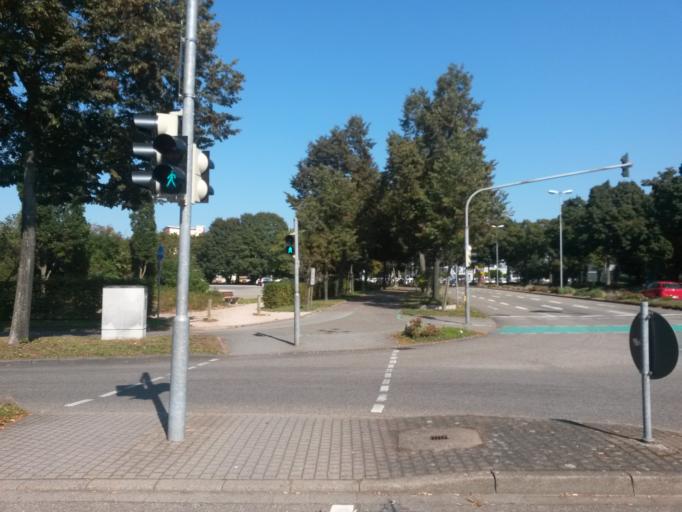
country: DE
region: Baden-Wuerttemberg
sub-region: Freiburg Region
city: Kehl
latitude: 48.5746
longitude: 7.8150
